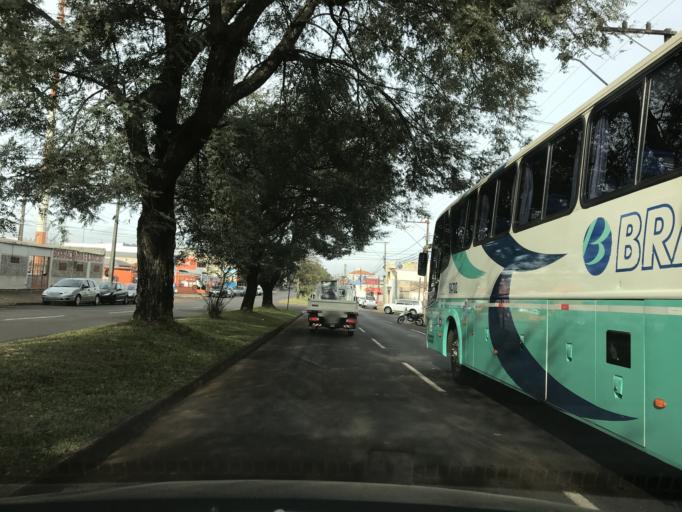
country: BR
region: Parana
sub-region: Cascavel
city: Cascavel
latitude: -24.9648
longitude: -53.4829
